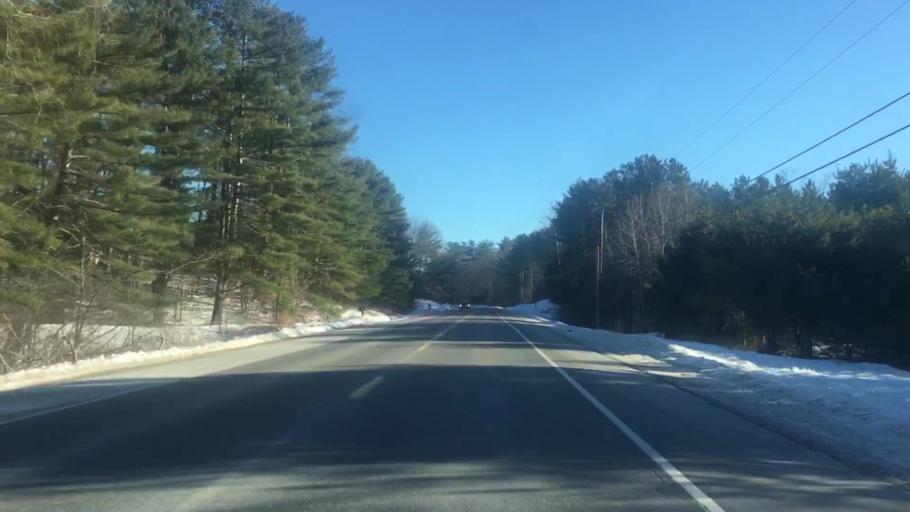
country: US
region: Maine
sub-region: Somerset County
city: Norridgewock
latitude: 44.7281
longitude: -69.8130
